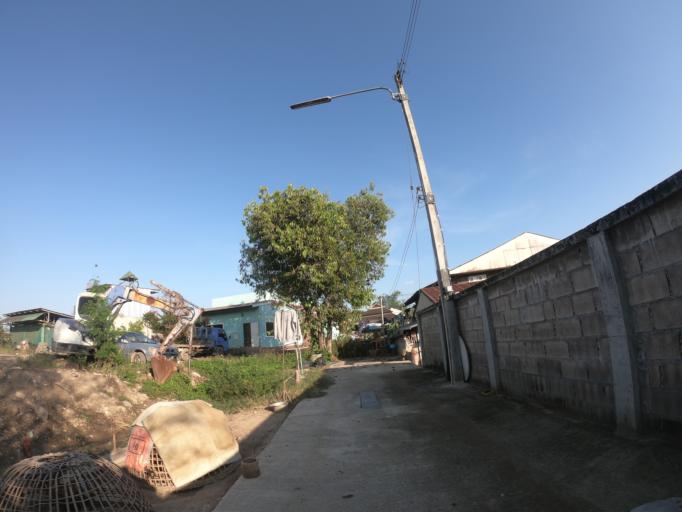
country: TH
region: Chiang Mai
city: Chiang Mai
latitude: 18.7433
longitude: 98.9826
